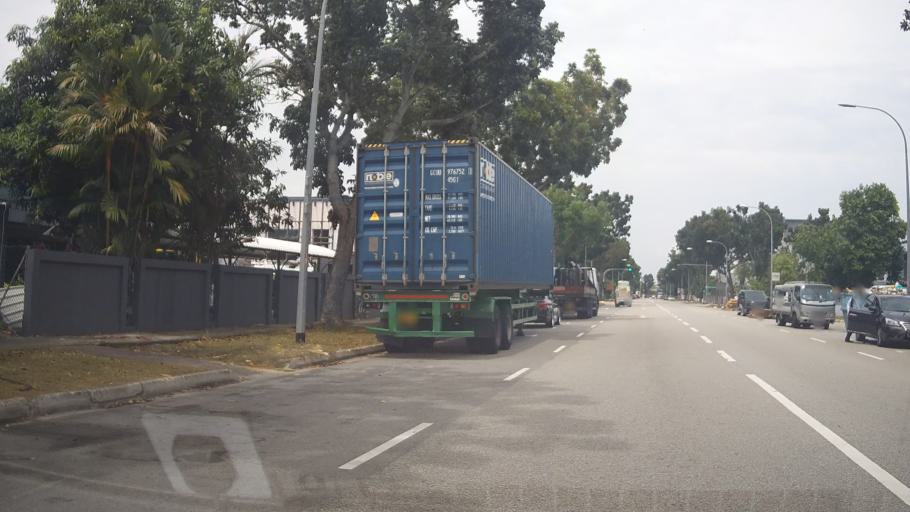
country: SG
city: Singapore
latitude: 1.3346
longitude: 103.9692
